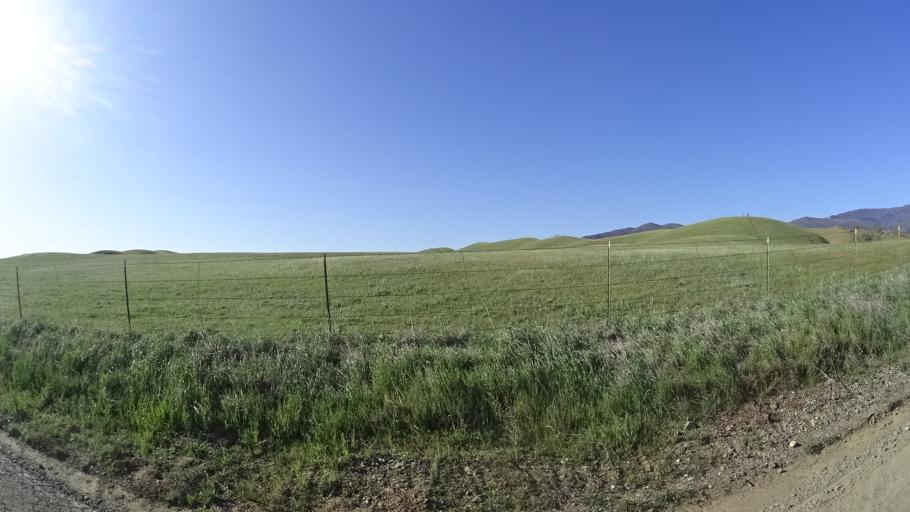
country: US
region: California
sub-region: Tehama County
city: Rancho Tehama Reserve
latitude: 39.7989
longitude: -122.5582
